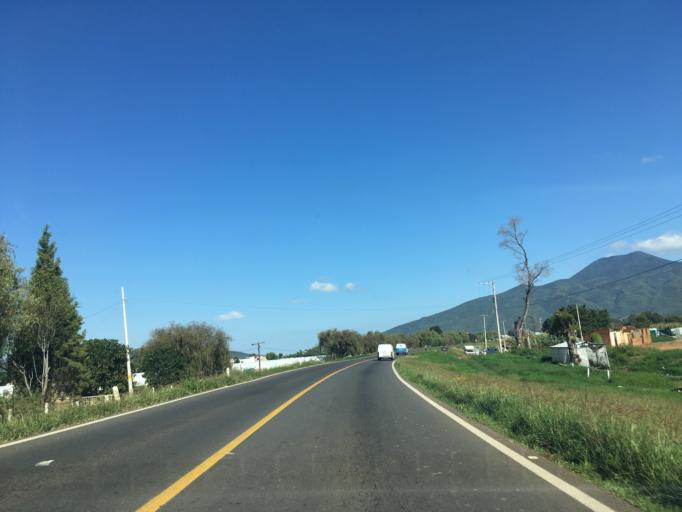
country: MX
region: Mexico
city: Tangancicuaro de Arista
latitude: 19.8733
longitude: -102.1973
